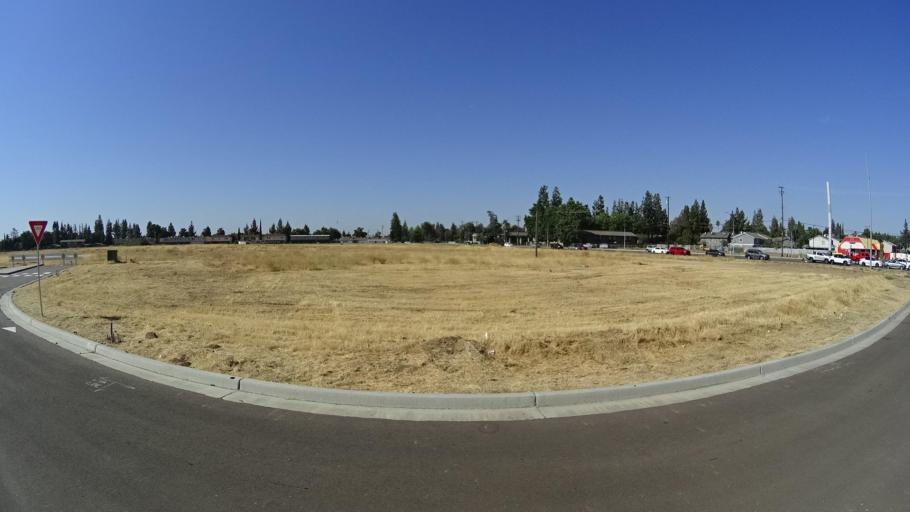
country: US
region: California
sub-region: Fresno County
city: Sunnyside
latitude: 36.7435
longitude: -119.6991
